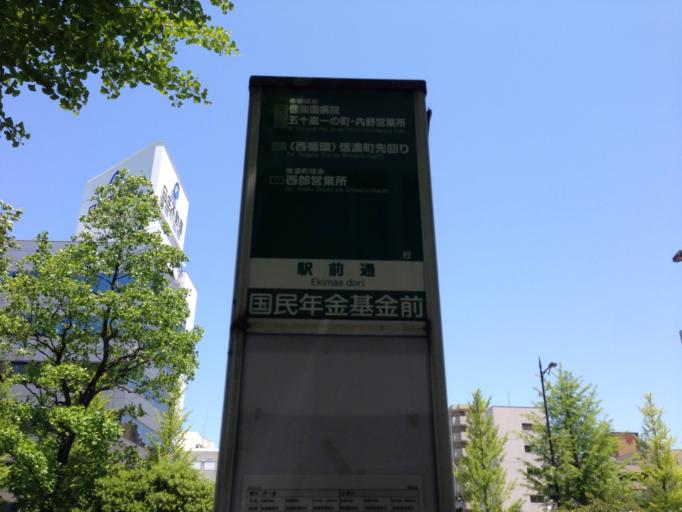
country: JP
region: Niigata
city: Niigata-shi
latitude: 37.9158
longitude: 139.0595
